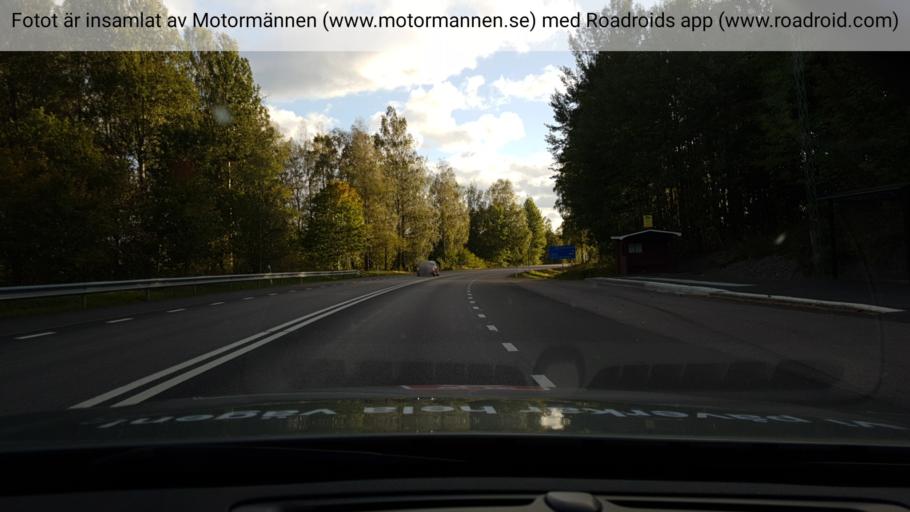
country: SE
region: Vaermland
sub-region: Karlstads Kommun
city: Molkom
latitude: 59.6001
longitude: 13.7371
